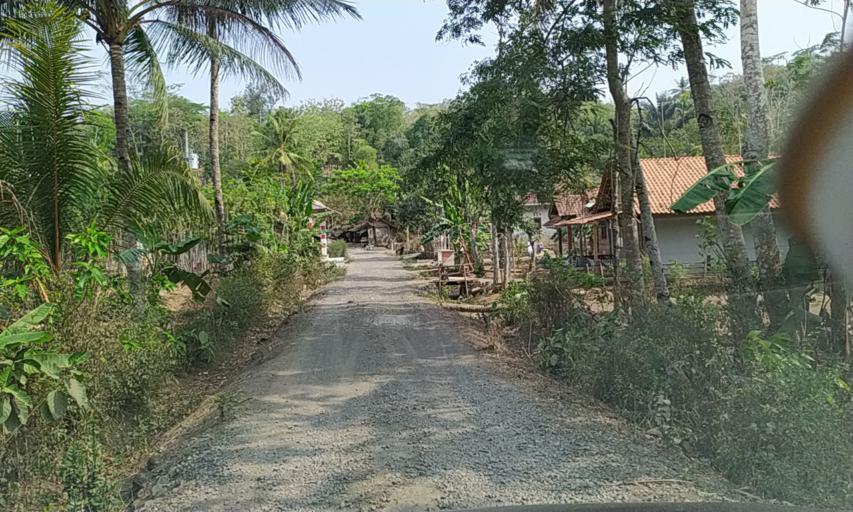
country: ID
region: Central Java
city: Karanggintung
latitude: -7.4749
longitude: 108.8922
